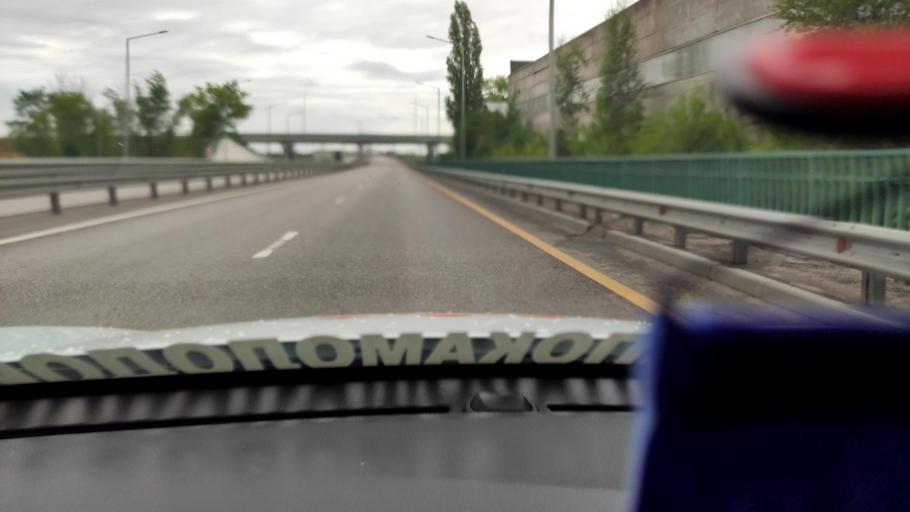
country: RU
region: Voronezj
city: Novaya Usman'
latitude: 51.6294
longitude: 39.3177
